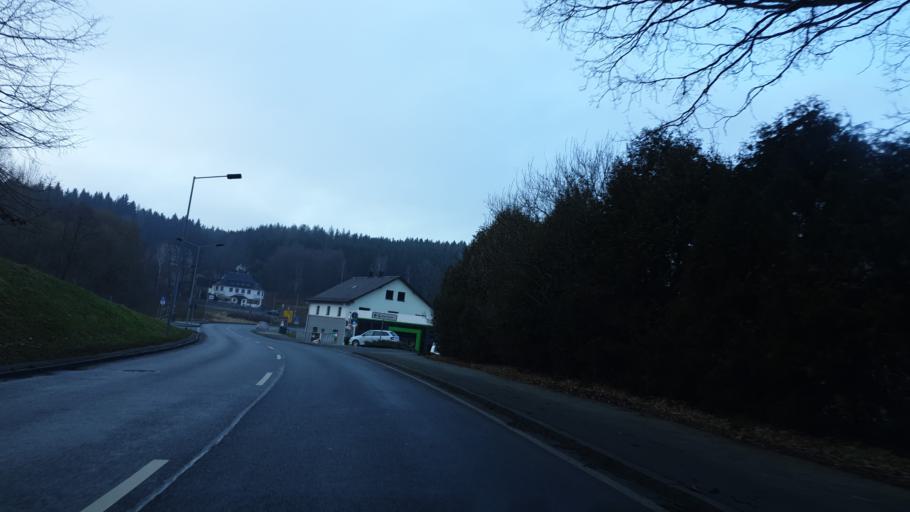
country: DE
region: Saxony
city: Adorf
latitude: 50.2993
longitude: 12.2548
